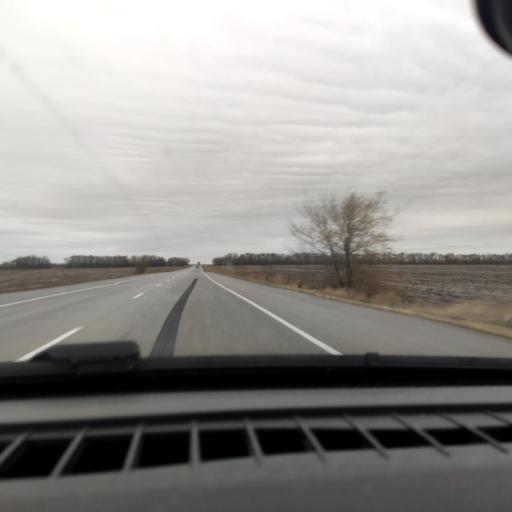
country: RU
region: Voronezj
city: Strelitsa
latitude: 51.4944
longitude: 38.9644
